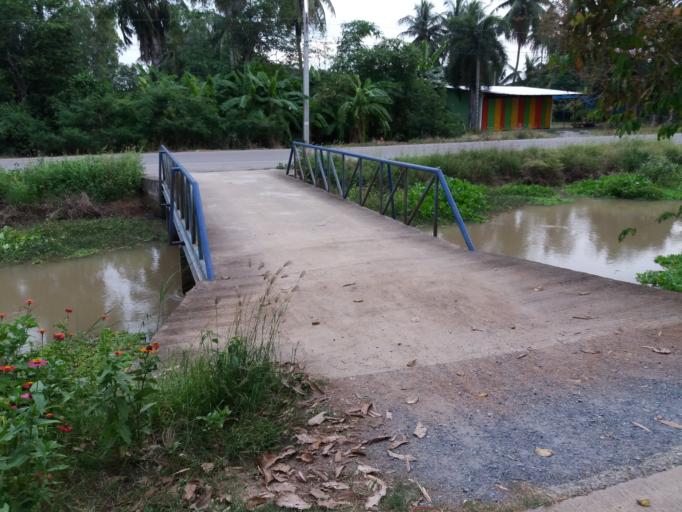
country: TH
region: Suphan Buri
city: Doem Bang Nang Buat
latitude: 14.9393
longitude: 100.1542
